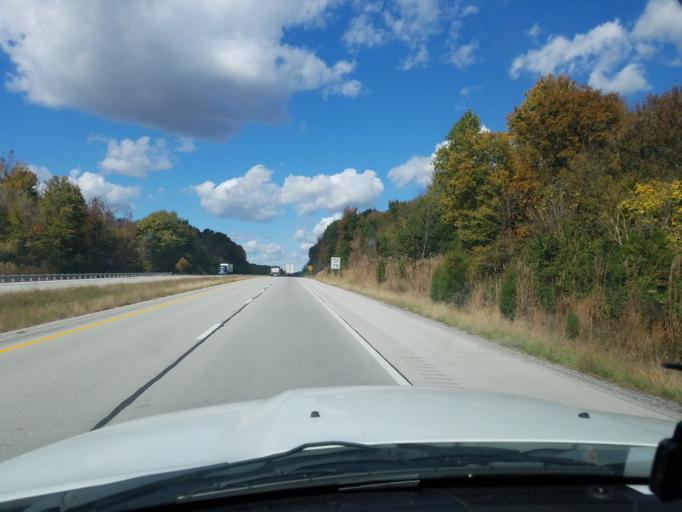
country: US
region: Kentucky
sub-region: Butler County
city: Morgantown
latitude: 37.2234
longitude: -86.7180
